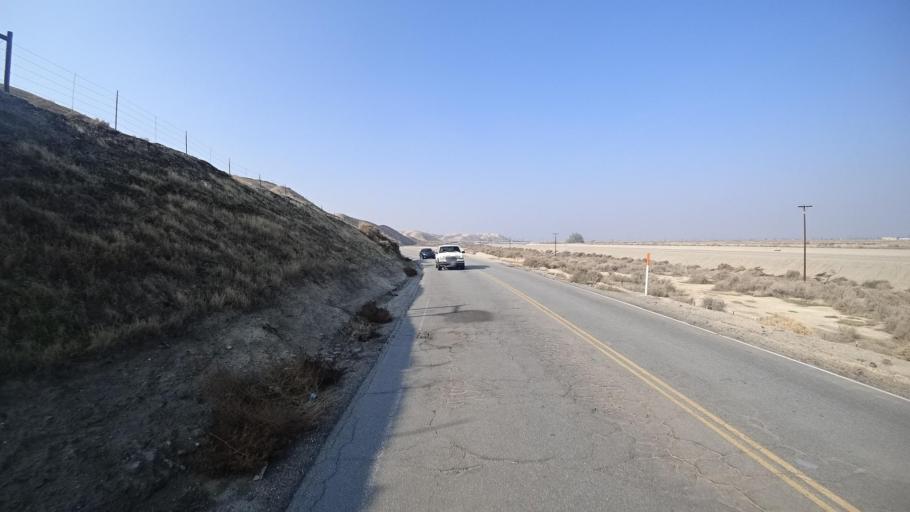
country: US
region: California
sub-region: Kern County
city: Ford City
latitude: 35.2713
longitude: -119.3154
